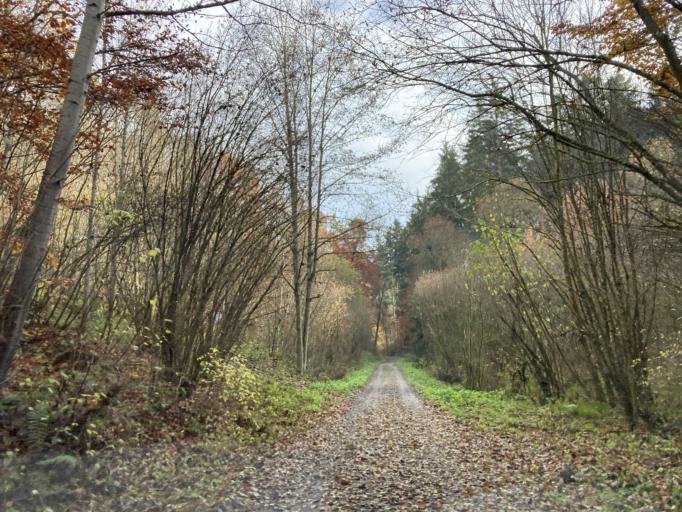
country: DE
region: Baden-Wuerttemberg
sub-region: Regierungsbezirk Stuttgart
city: Bondorf
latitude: 48.4791
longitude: 8.8243
